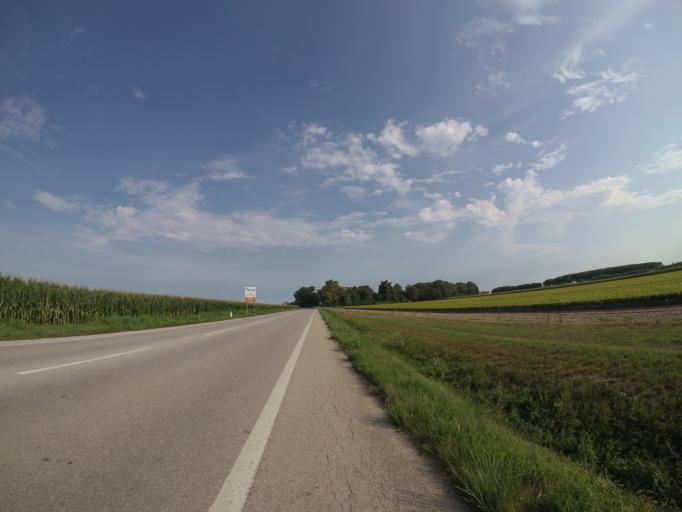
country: IT
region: Friuli Venezia Giulia
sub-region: Provincia di Udine
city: Varmo
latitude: 45.9244
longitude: 12.9878
